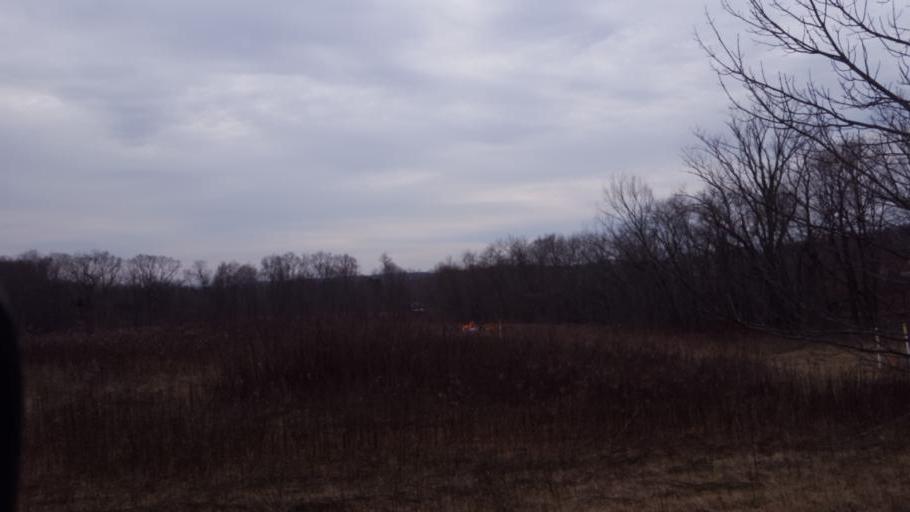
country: US
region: Ohio
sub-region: Ashland County
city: Loudonville
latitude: 40.7144
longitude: -82.3150
